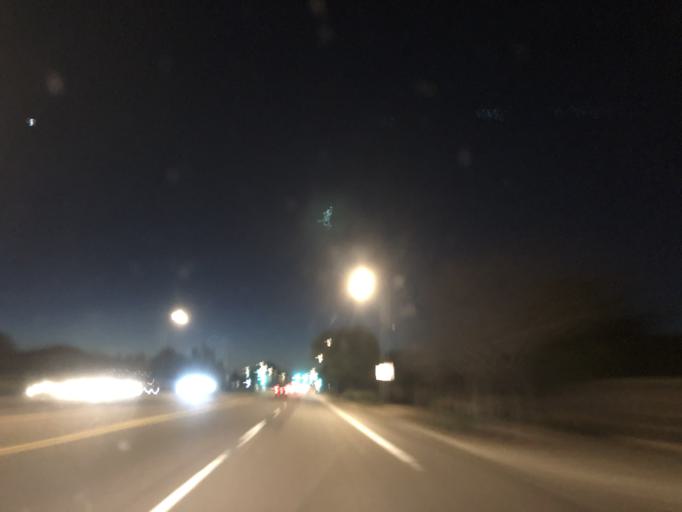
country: US
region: Arizona
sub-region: Maricopa County
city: Tolleson
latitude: 33.4224
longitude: -112.2442
